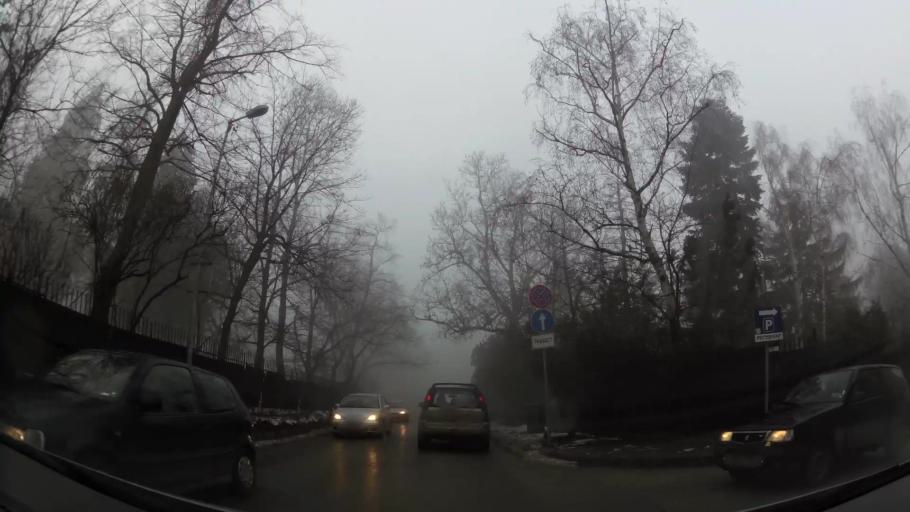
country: BG
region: Sofia-Capital
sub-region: Stolichna Obshtina
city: Sofia
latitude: 42.6544
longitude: 23.2505
